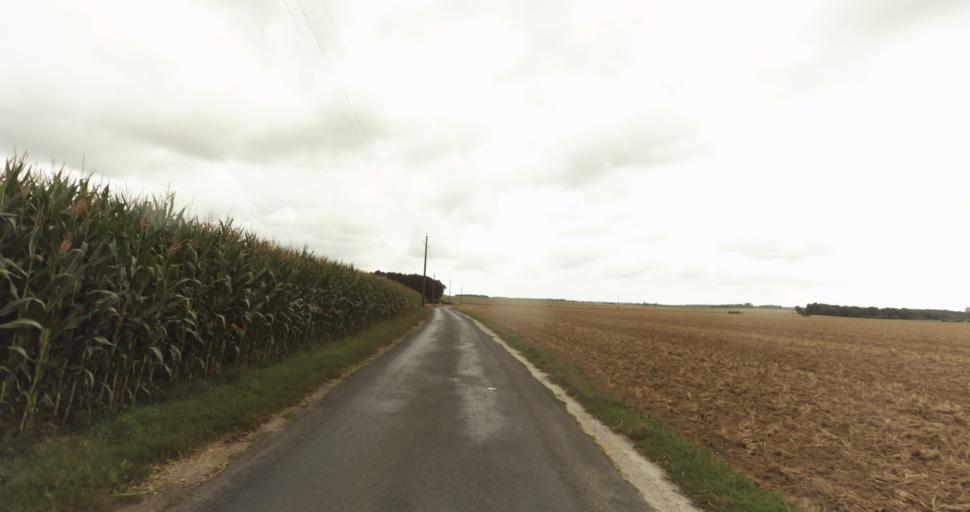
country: FR
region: Haute-Normandie
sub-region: Departement de l'Eure
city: Menilles
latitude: 49.0102
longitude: 1.2796
